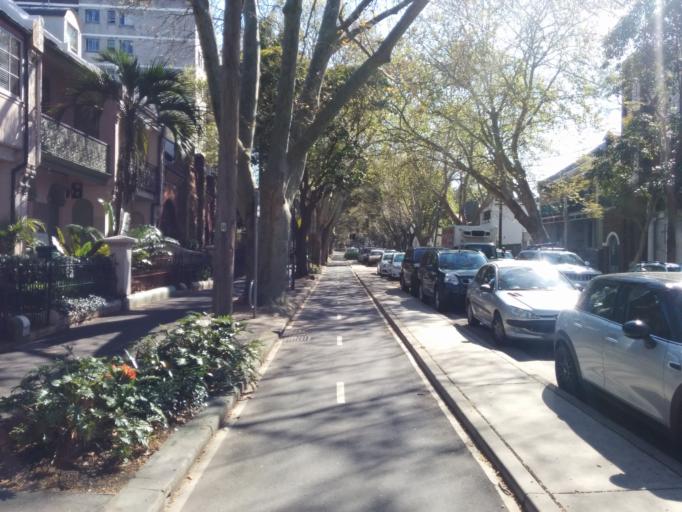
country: AU
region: New South Wales
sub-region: City of Sydney
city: Redfern
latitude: -33.8913
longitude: 151.2146
